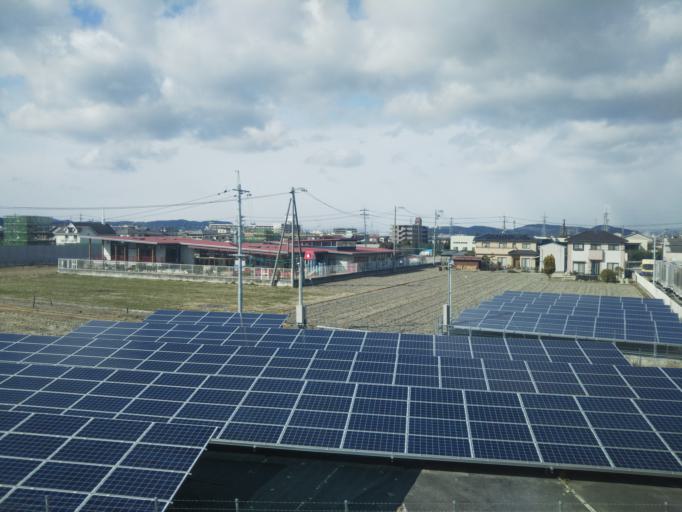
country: JP
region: Okayama
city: Okayama-shi
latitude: 34.6148
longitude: 133.8827
